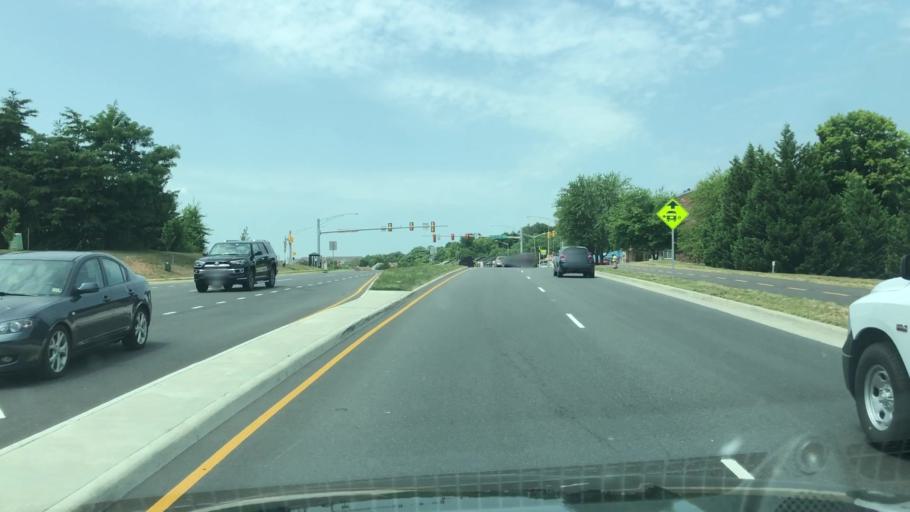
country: US
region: Virginia
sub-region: Stafford County
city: Falmouth
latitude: 38.3158
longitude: -77.4961
